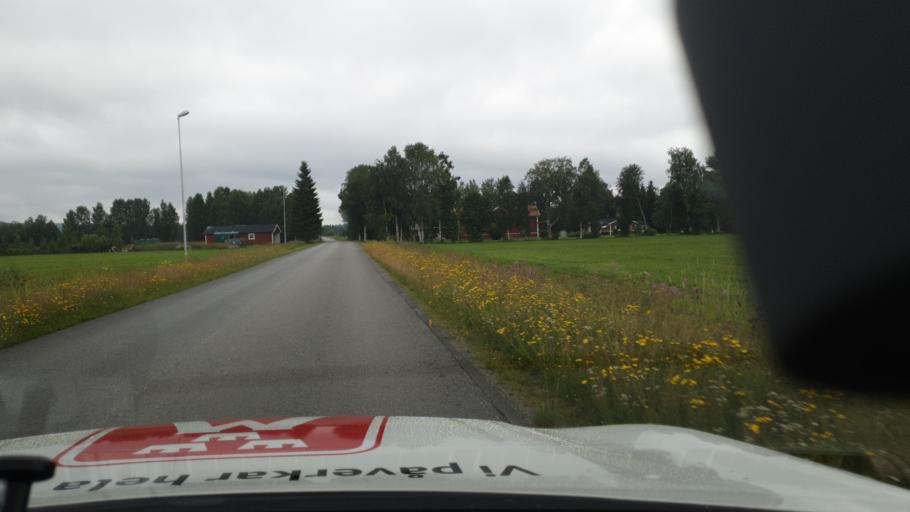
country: SE
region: Vaesterbotten
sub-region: Vannas Kommun
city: Vannasby
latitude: 63.9534
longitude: 19.8685
